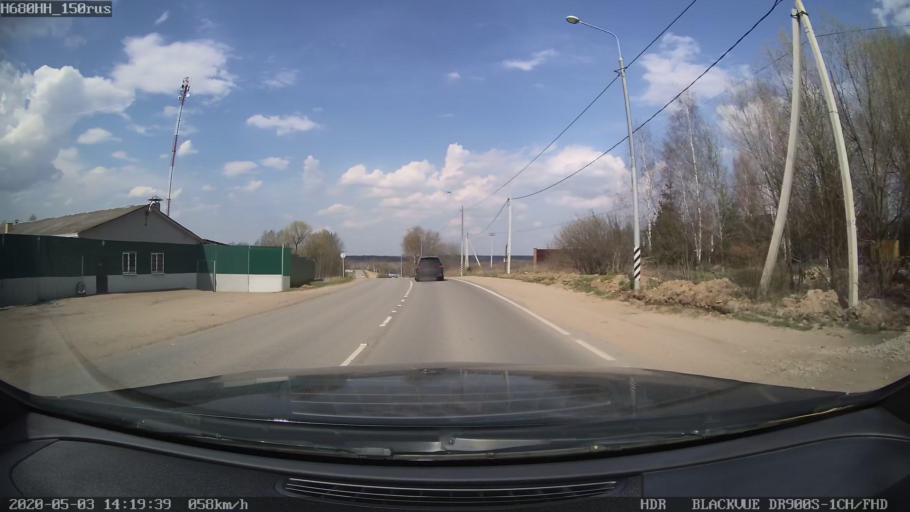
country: RU
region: Moskovskaya
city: Solnechnogorsk
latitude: 56.2329
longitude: 36.9692
